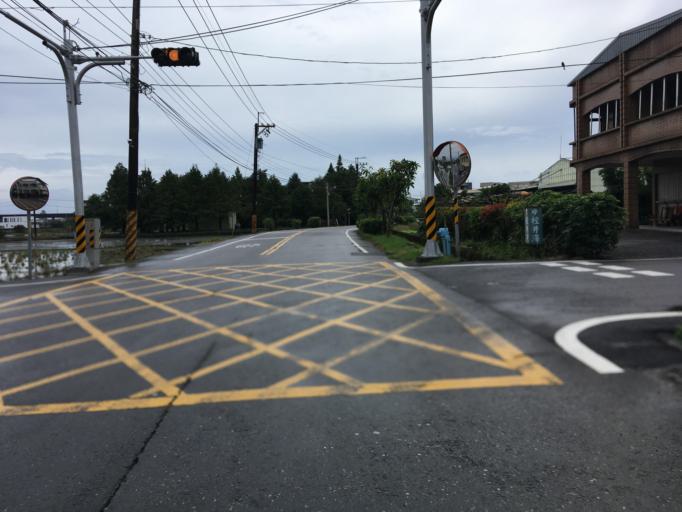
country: TW
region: Taiwan
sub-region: Yilan
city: Yilan
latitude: 24.6674
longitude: 121.7903
